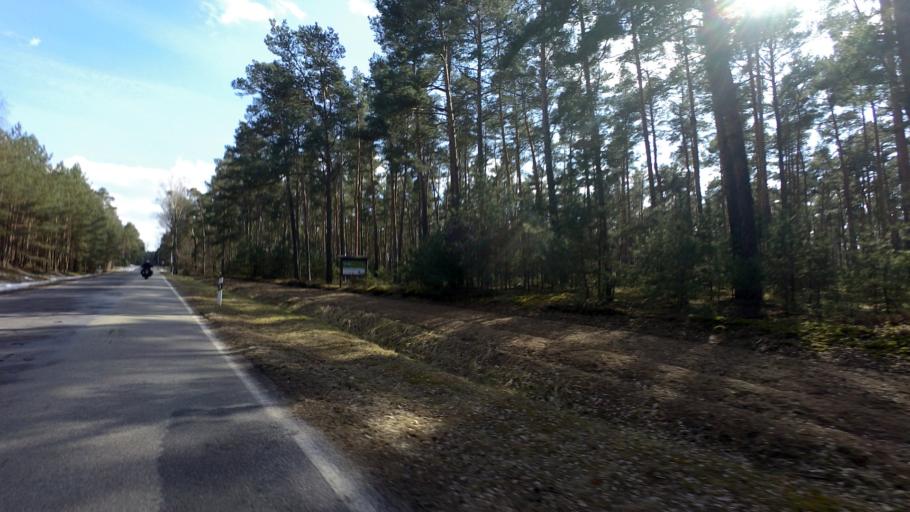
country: DE
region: Brandenburg
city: Marienwerder
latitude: 52.8056
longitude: 13.5871
